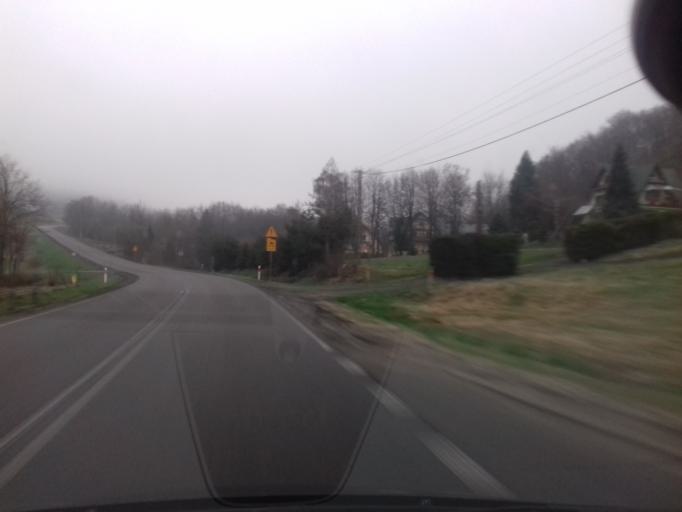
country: PL
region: Lesser Poland Voivodeship
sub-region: Powiat limanowski
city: Skrzydlna
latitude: 49.7022
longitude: 20.1940
